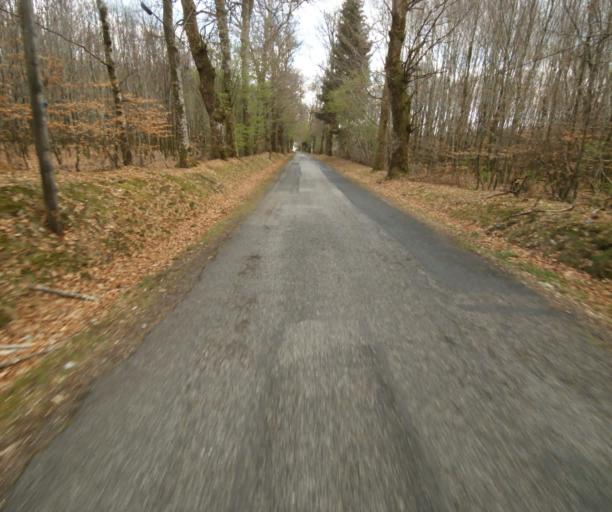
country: FR
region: Limousin
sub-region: Departement de la Correze
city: Correze
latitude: 45.2601
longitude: 1.9100
